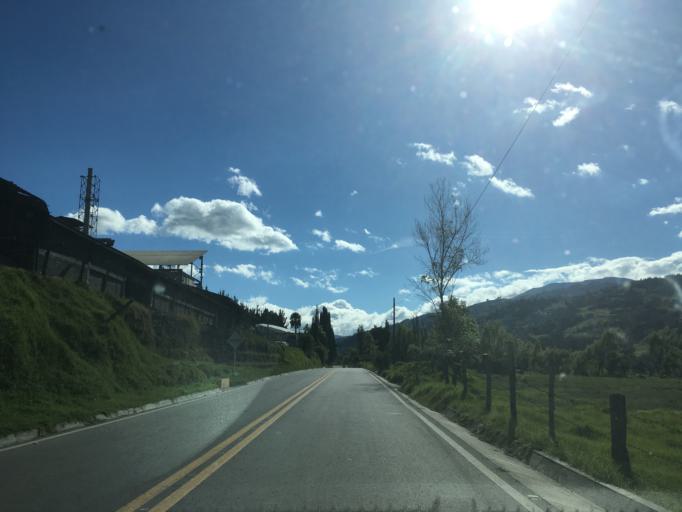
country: CO
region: Boyaca
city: Pesca
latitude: 5.5752
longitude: -73.0406
